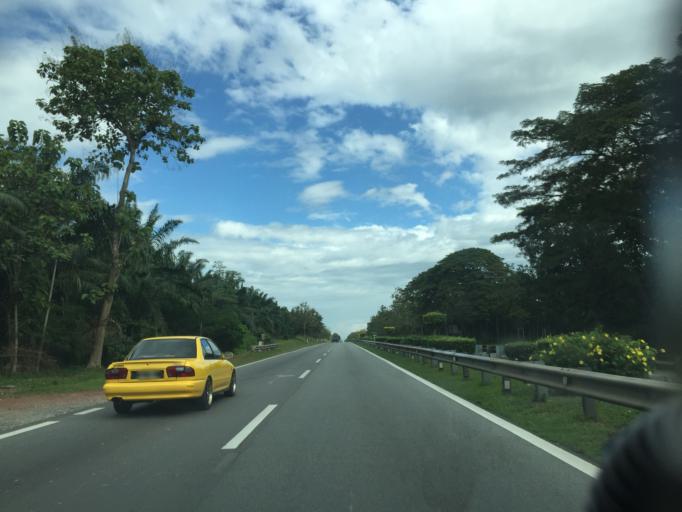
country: MY
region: Kedah
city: Jitra
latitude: 6.3735
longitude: 100.4237
